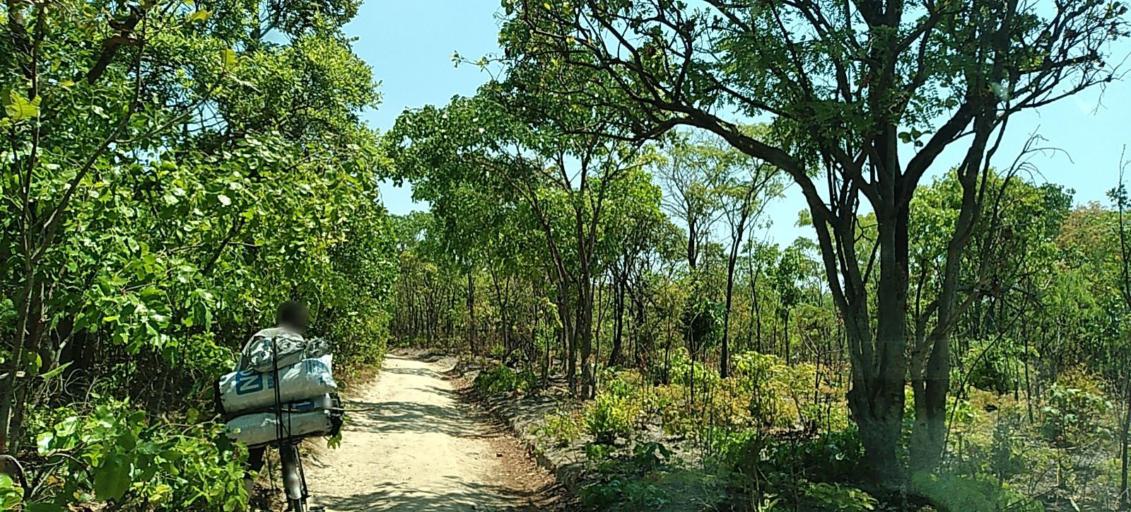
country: ZM
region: Copperbelt
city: Luanshya
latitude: -12.9757
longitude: 28.3307
